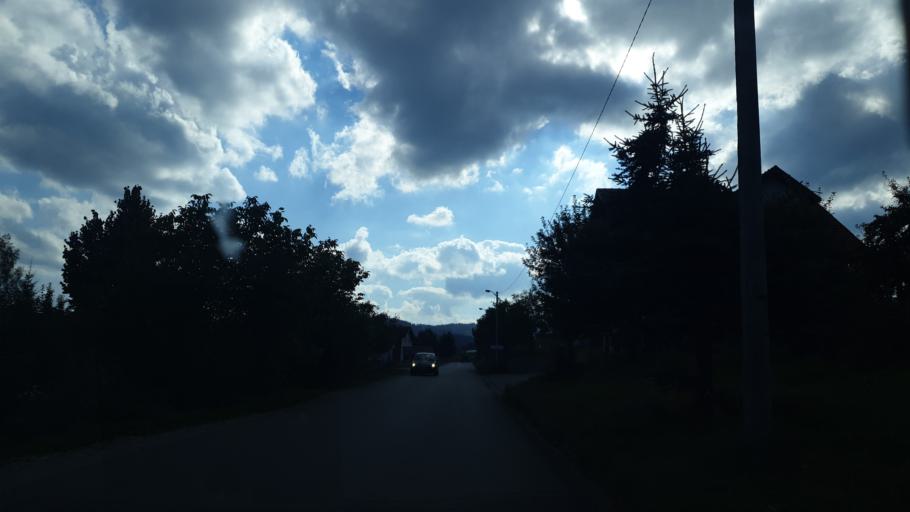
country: RS
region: Central Serbia
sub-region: Zlatiborski Okrug
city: Nova Varos
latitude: 43.4274
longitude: 19.8788
